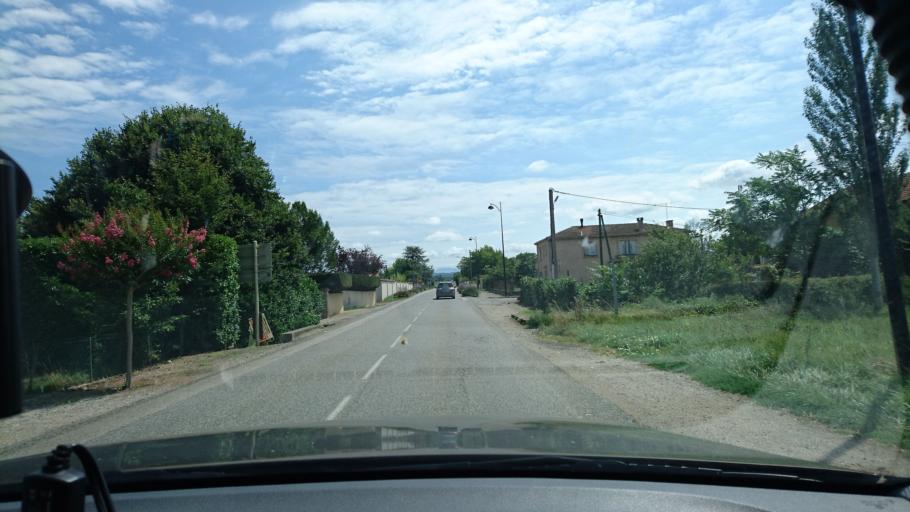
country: FR
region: Midi-Pyrenees
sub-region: Departement de la Haute-Garonne
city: Gaillac-Toulza
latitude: 43.1714
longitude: 1.4108
